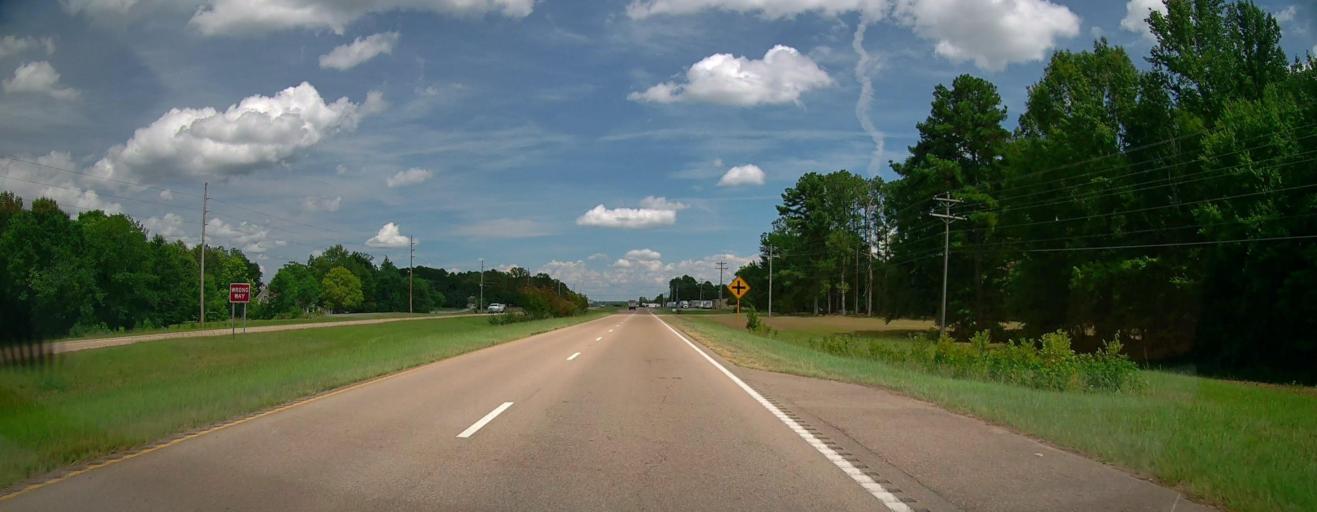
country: US
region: Mississippi
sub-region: Lee County
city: Shannon
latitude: 34.1082
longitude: -88.6785
